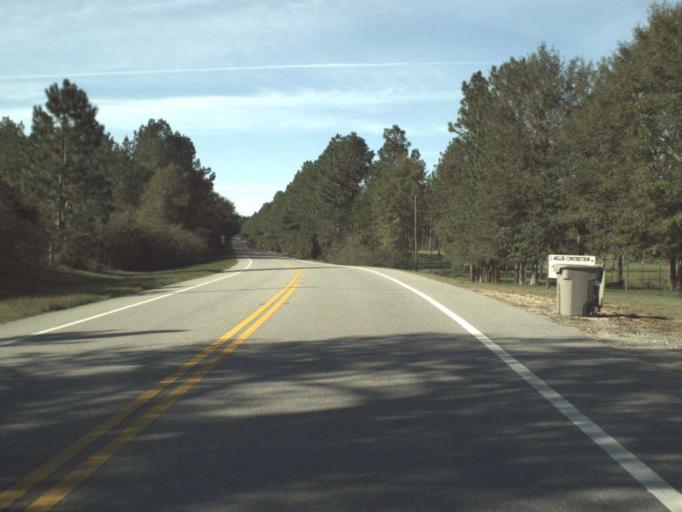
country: US
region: Florida
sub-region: Escambia County
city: Molino
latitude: 30.8125
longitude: -87.4271
